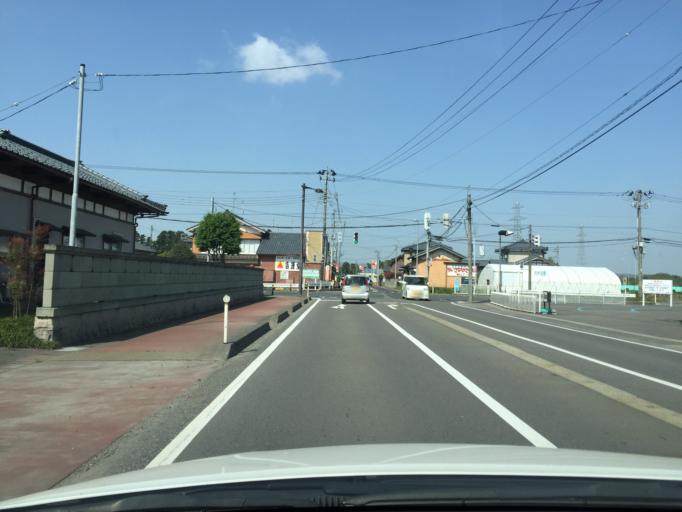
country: JP
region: Niigata
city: Gosen
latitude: 37.7477
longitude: 139.2043
